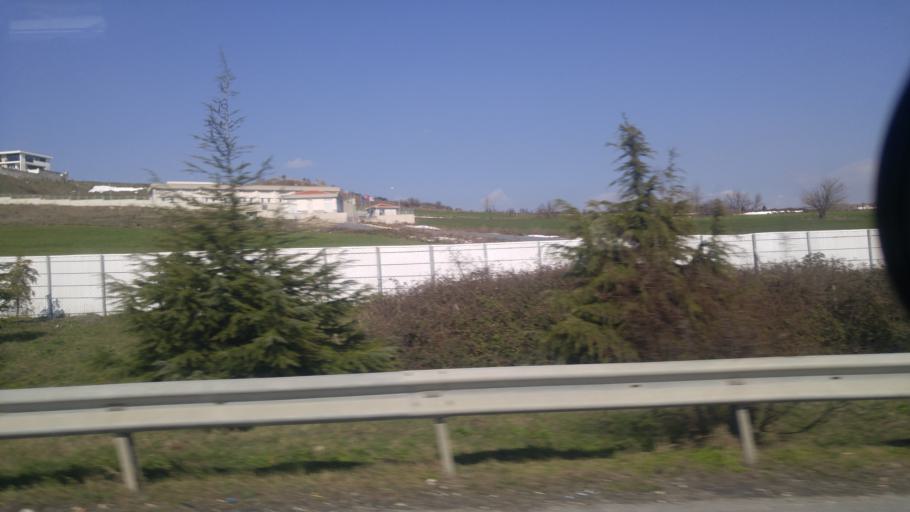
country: TR
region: Istanbul
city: Selimpasa
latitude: 41.0675
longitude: 28.3924
